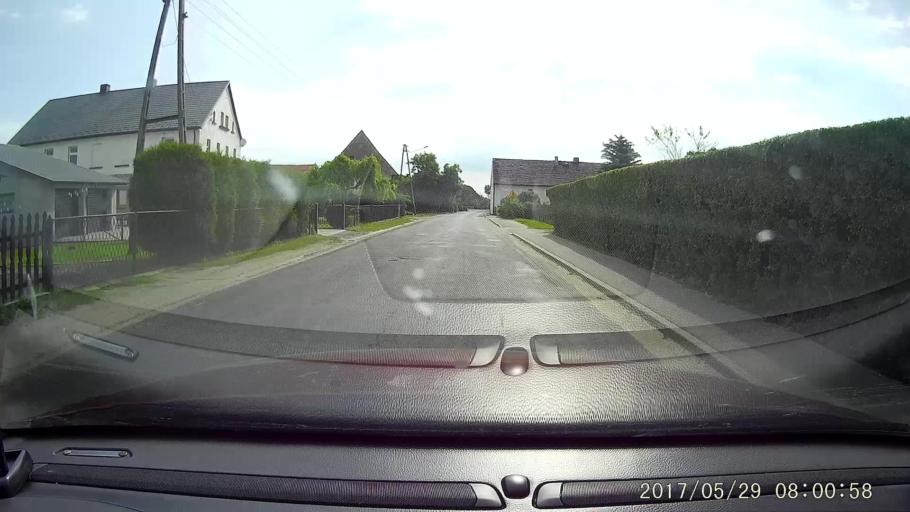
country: PL
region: Lower Silesian Voivodeship
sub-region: Powiat zlotoryjski
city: Olszanica
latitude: 51.2066
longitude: 15.8063
